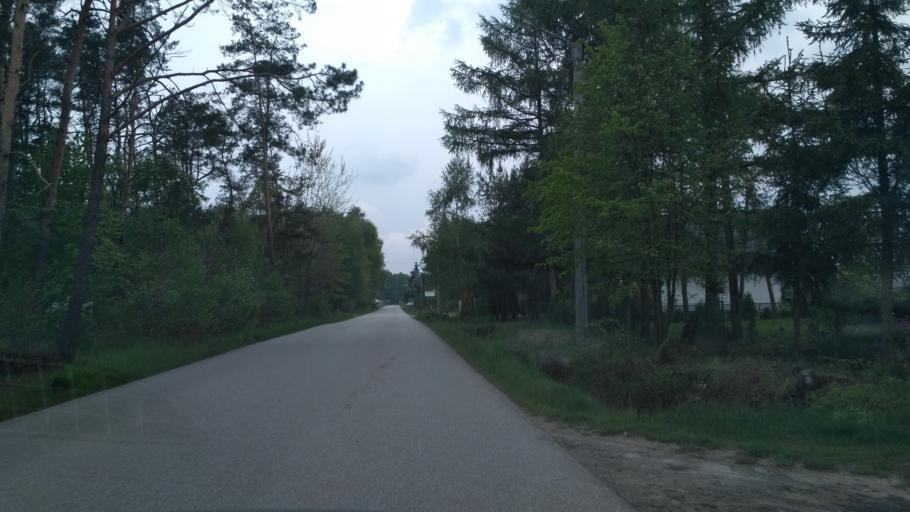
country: PL
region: Subcarpathian Voivodeship
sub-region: Powiat kolbuszowski
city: Kolbuszowa
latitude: 50.1980
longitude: 21.7780
